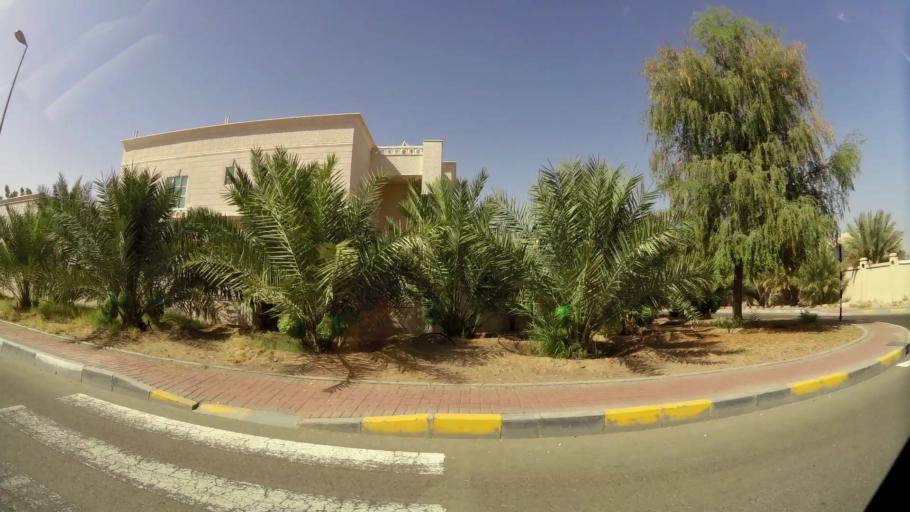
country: OM
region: Al Buraimi
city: Al Buraymi
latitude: 24.3163
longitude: 55.8118
